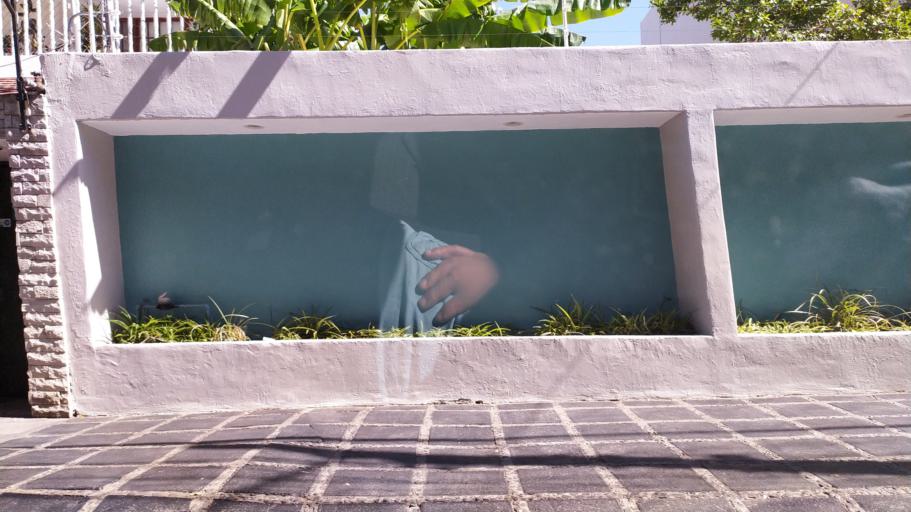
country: MX
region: Jalisco
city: Guadalajara
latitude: 20.6911
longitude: -103.3921
